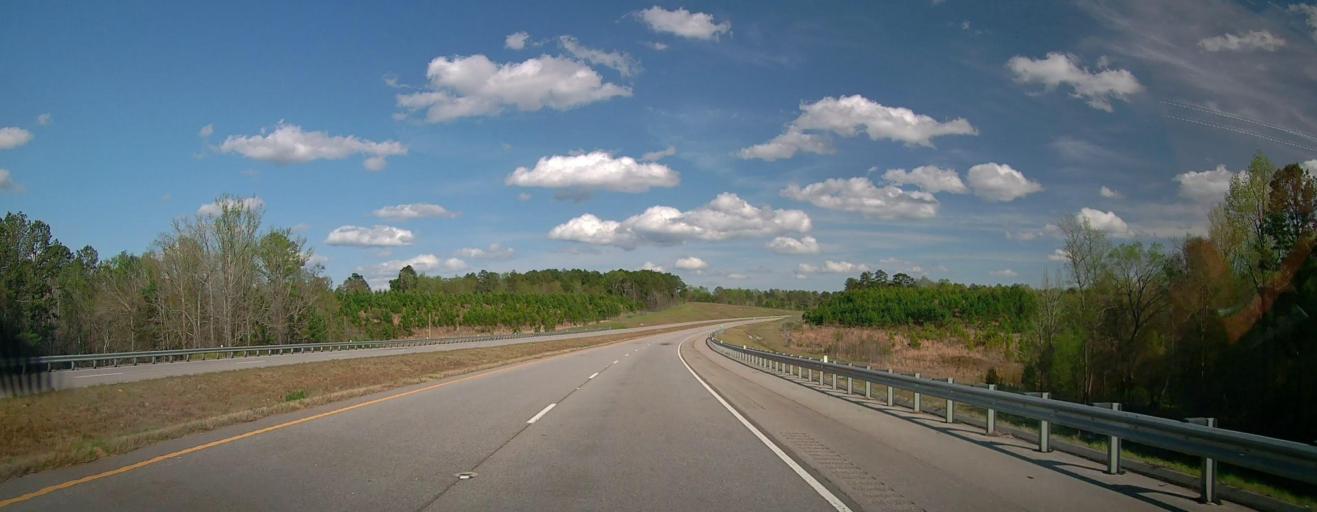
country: US
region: Georgia
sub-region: Baldwin County
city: Hardwick
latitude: 33.0412
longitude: -83.1253
